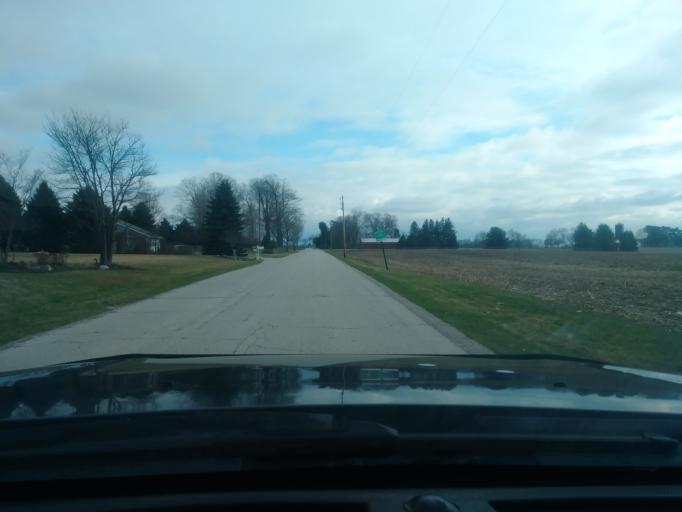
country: US
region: Indiana
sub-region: LaPorte County
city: LaPorte
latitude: 41.5710
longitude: -86.7982
